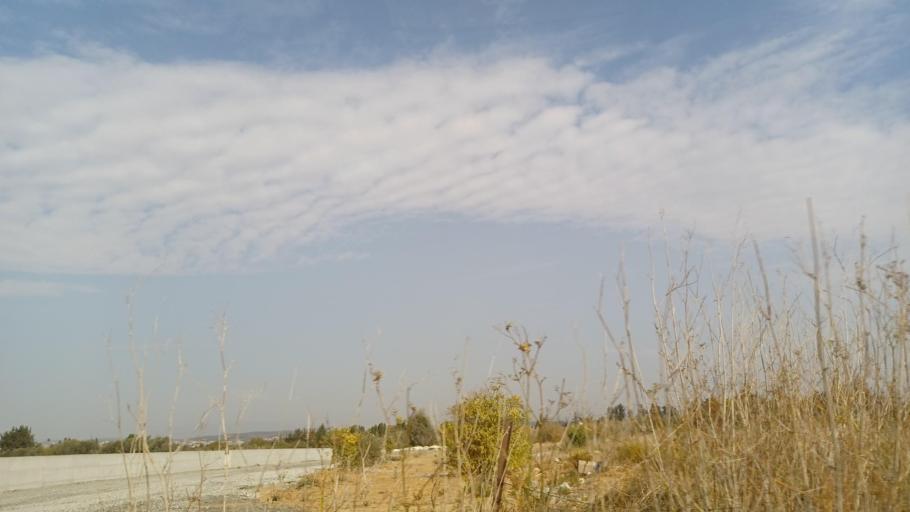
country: CY
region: Larnaka
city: Kolossi
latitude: 34.6645
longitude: 32.9468
